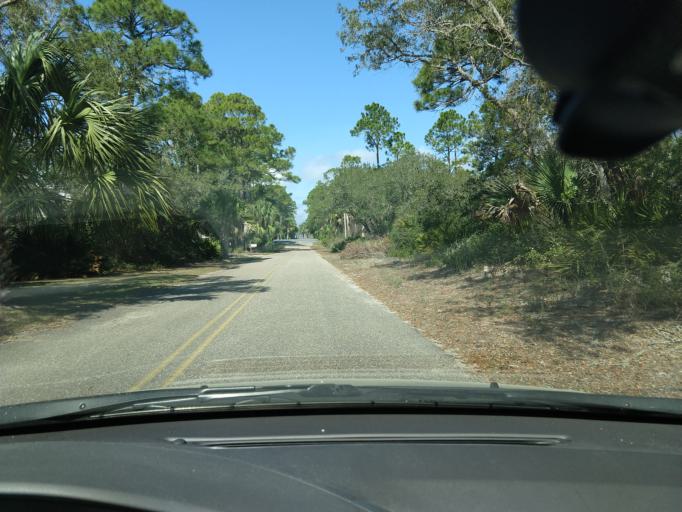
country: US
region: Florida
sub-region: Gulf County
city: Port Saint Joe
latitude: 29.6789
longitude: -85.2330
